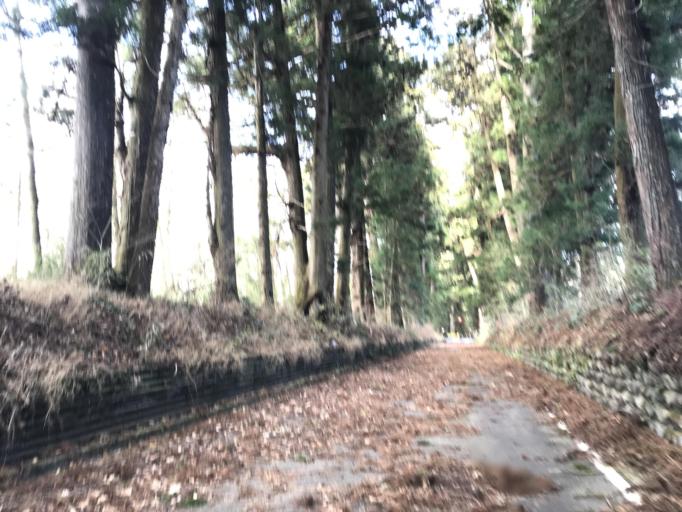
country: JP
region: Tochigi
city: Imaichi
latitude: 36.6832
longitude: 139.7189
